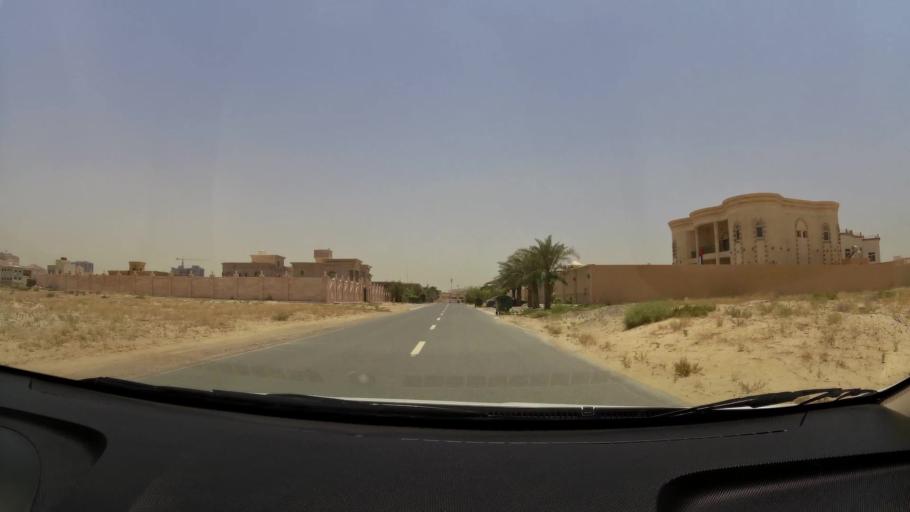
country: AE
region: Ajman
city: Ajman
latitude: 25.4103
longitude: 55.5025
